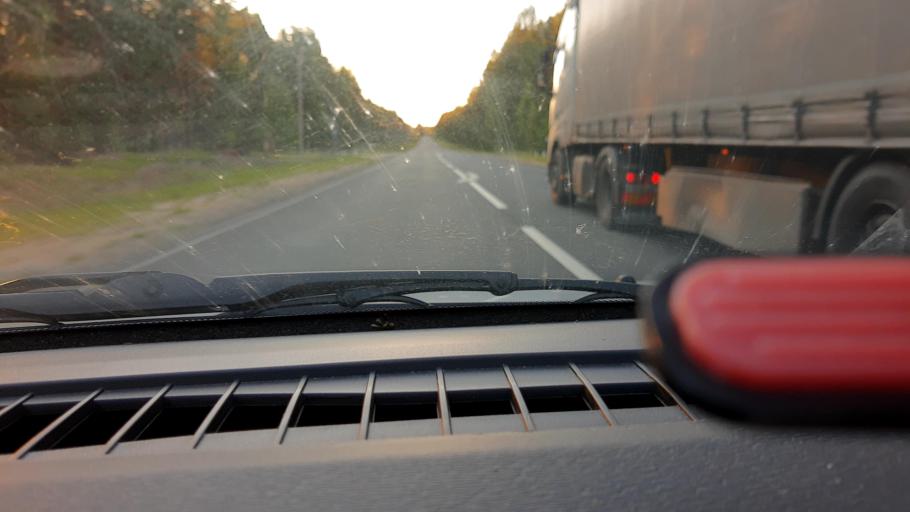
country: RU
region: Nizjnij Novgorod
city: Uren'
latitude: 57.3577
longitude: 45.7004
